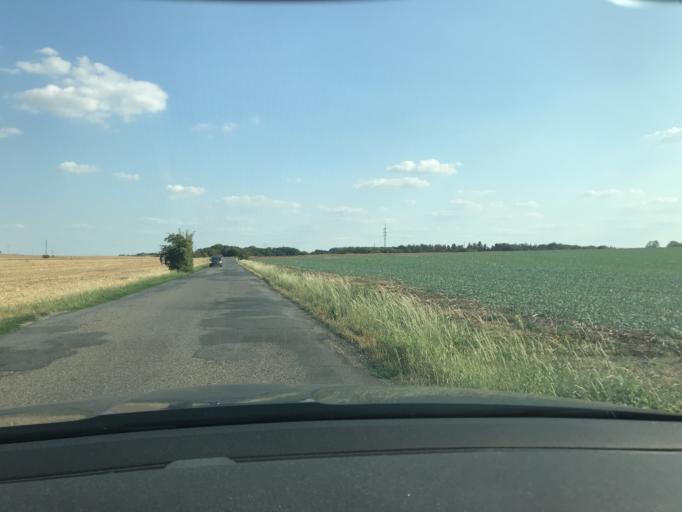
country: CZ
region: Central Bohemia
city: Kralupy nad Vltavou
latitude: 50.2236
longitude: 14.3236
